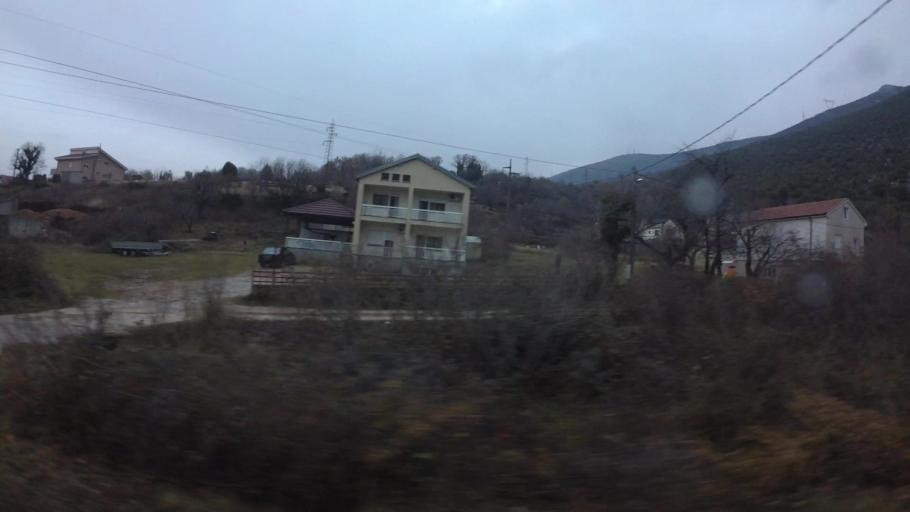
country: BA
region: Federation of Bosnia and Herzegovina
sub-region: Hercegovacko-Bosanski Kanton
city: Mostar
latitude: 43.3686
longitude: 17.8075
